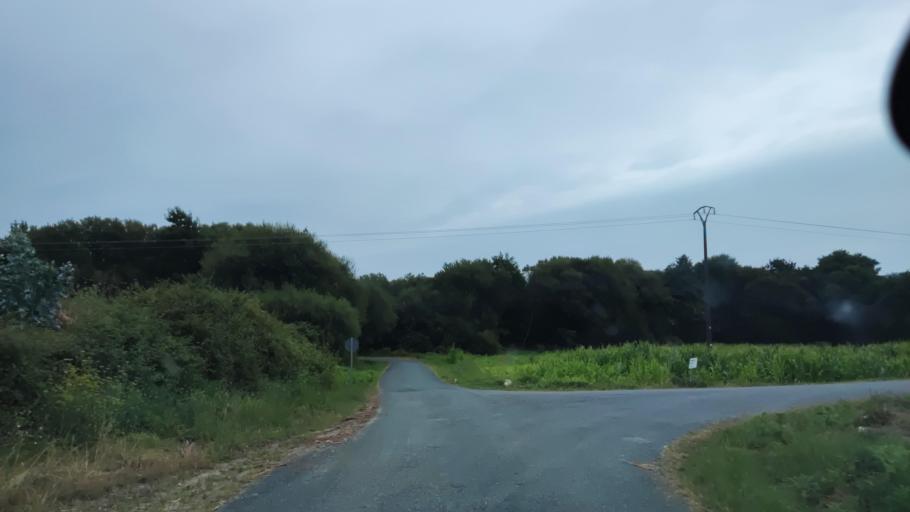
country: ES
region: Galicia
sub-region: Provincia da Coruna
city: Padron
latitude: 42.7249
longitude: -8.6756
